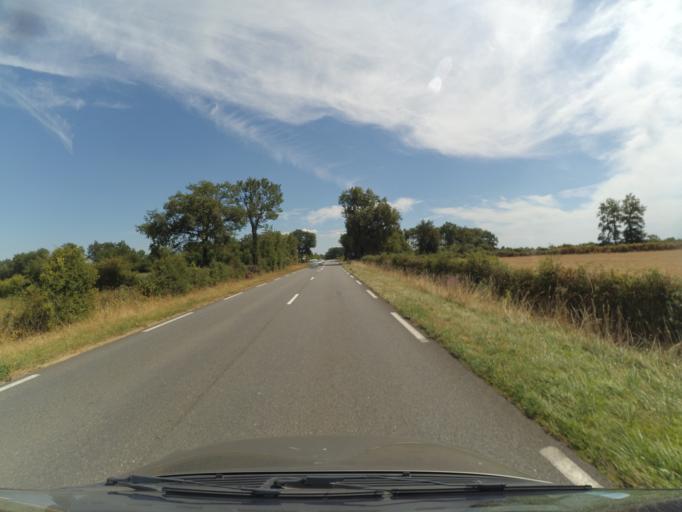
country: FR
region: Poitou-Charentes
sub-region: Departement de la Charente
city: Confolens
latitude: 46.0429
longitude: 0.6262
